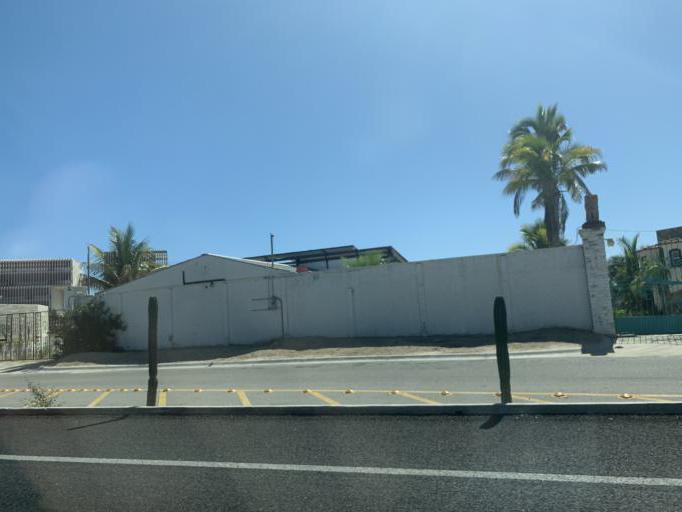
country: MX
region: Baja California Sur
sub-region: Los Cabos
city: San Jose del Cabo
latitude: 22.9729
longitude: -109.7845
